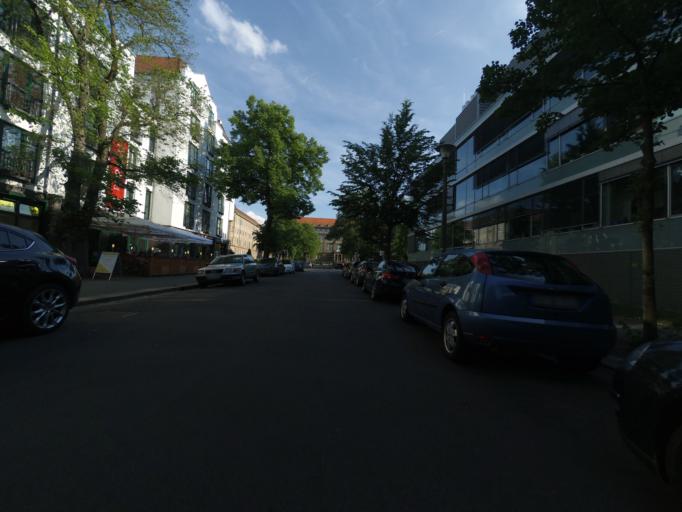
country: DE
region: Saxony
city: Albertstadt
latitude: 51.0541
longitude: 13.7841
